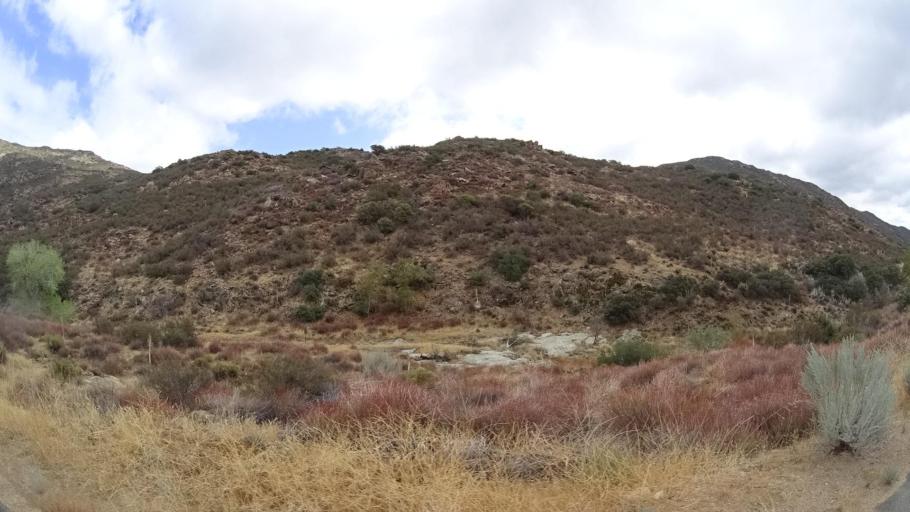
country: US
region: California
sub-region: San Diego County
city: Pine Valley
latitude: 32.7648
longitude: -116.4521
